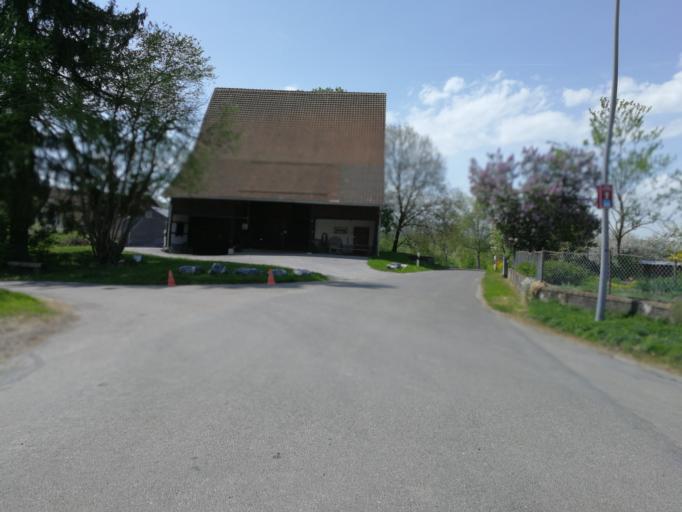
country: CH
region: Zurich
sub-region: Bezirk Hinwil
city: Gossau
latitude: 47.2946
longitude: 8.7555
